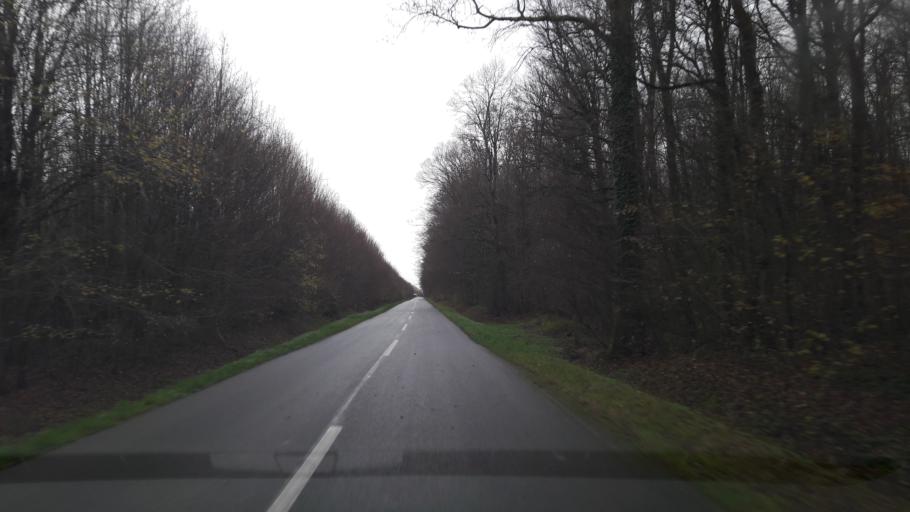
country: HR
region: Osjecko-Baranjska
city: Velimirovac
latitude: 45.6296
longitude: 18.0940
